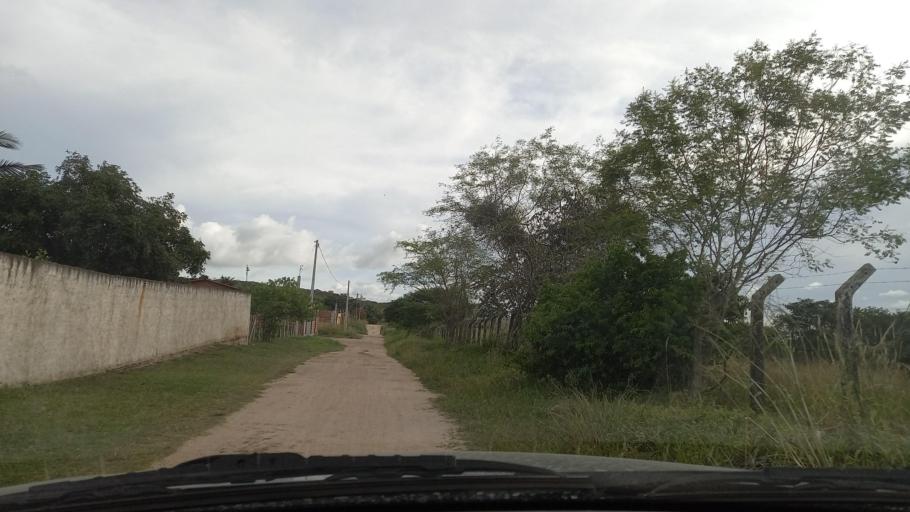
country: BR
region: Pernambuco
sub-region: Gravata
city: Gravata
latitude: -8.1984
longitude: -35.5360
